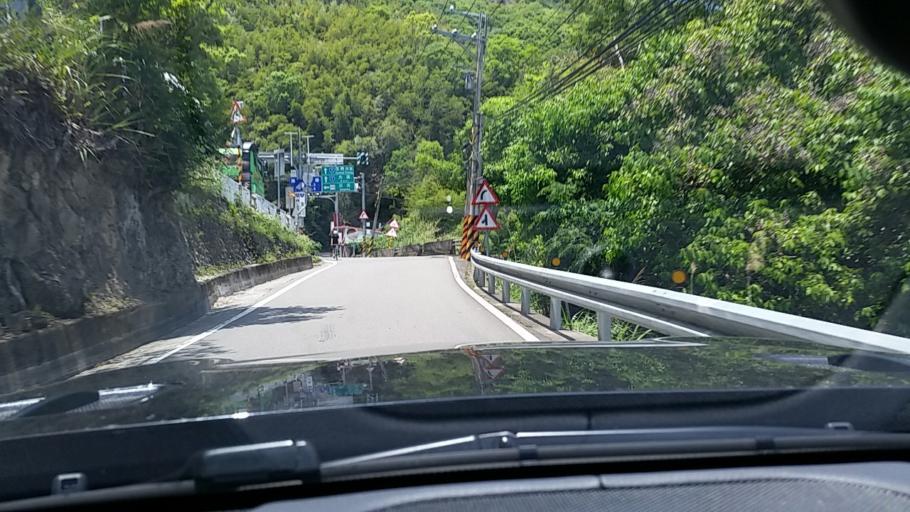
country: TW
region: Taiwan
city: Daxi
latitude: 24.6924
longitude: 121.3746
